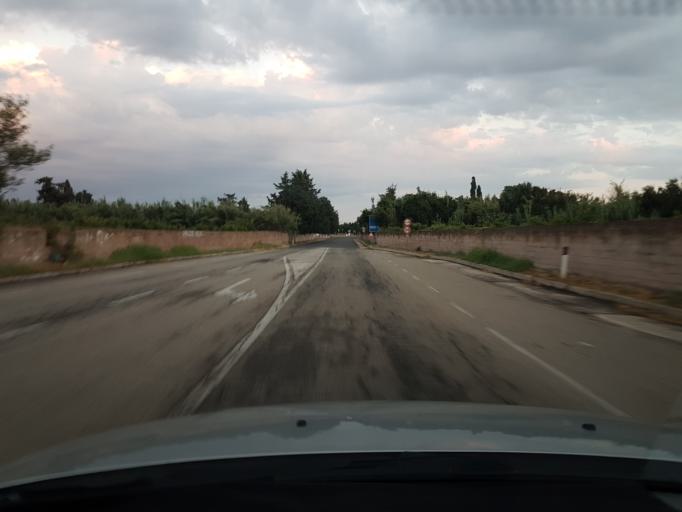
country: IT
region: Sardinia
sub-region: Provincia di Oristano
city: Milis
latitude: 40.0458
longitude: 8.6320
